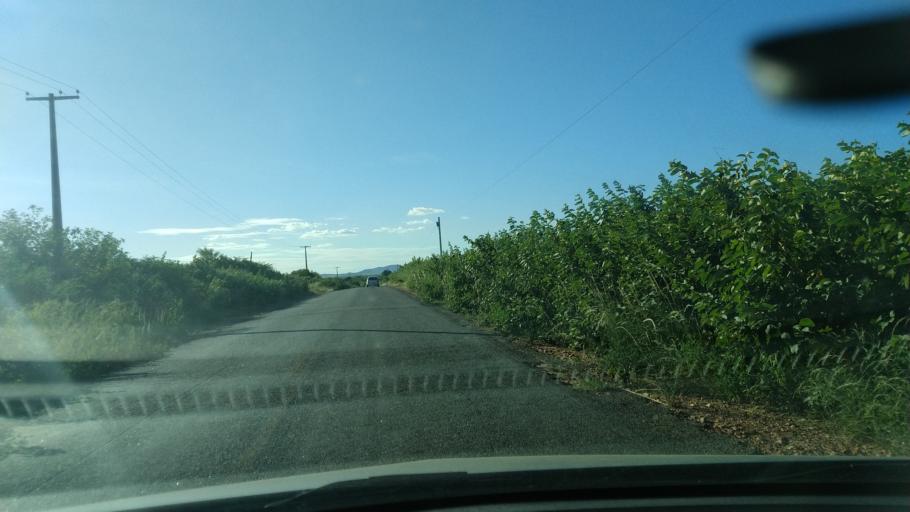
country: BR
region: Rio Grande do Norte
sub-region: Sao Jose Do Campestre
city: Sao Jose do Campestre
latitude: -6.4071
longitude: -35.6533
